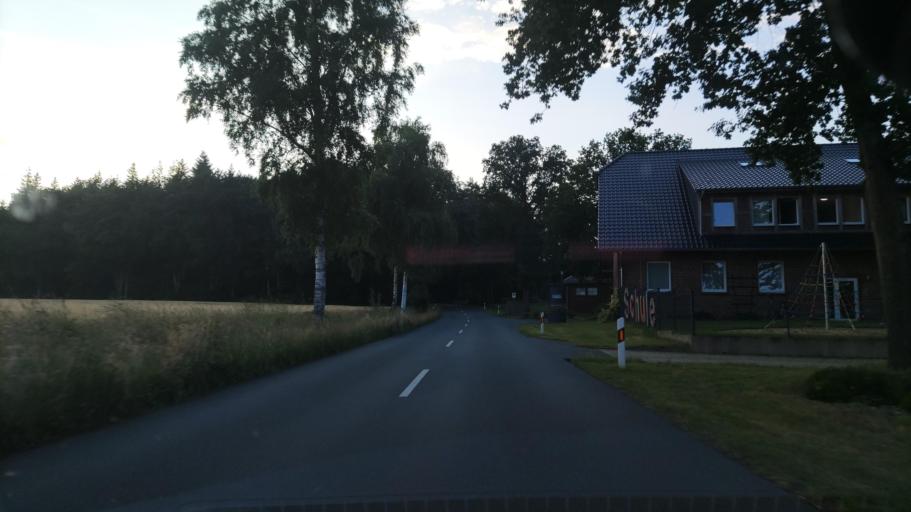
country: DE
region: Lower Saxony
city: Bispingen
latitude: 53.1217
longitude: 10.0539
